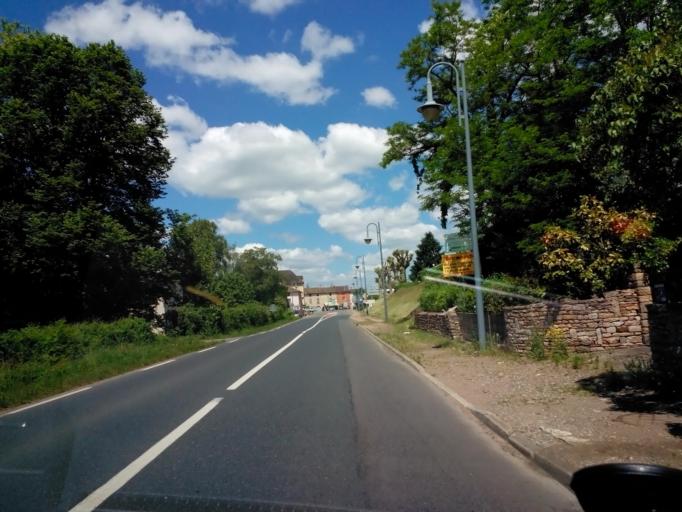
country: FR
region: Bourgogne
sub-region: Departement de Saone-et-Loire
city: Cluny
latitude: 46.4235
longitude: 4.6648
